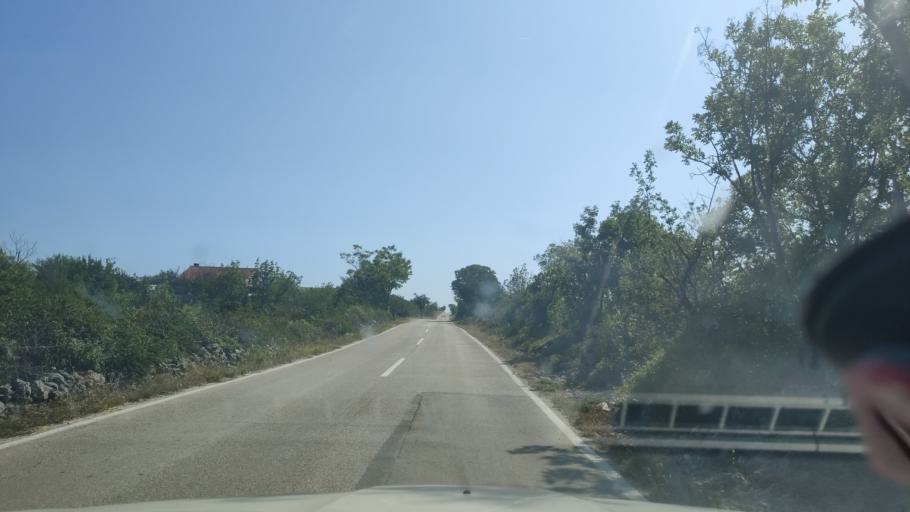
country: HR
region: Sibensko-Kniniska
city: Kistanje
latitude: 43.9136
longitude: 15.9443
